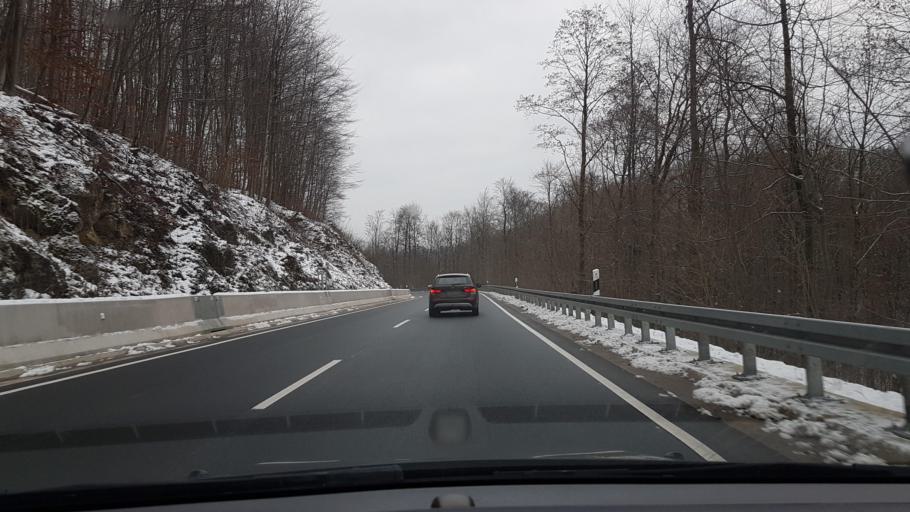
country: DE
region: Lower Saxony
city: Bad Grund
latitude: 51.8199
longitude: 10.2362
